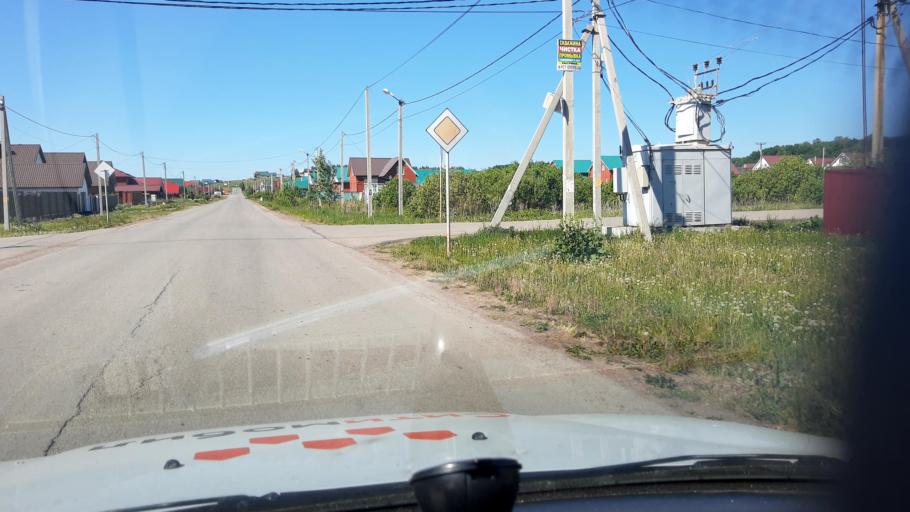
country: RU
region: Bashkortostan
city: Kabakovo
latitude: 54.6608
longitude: 56.2145
